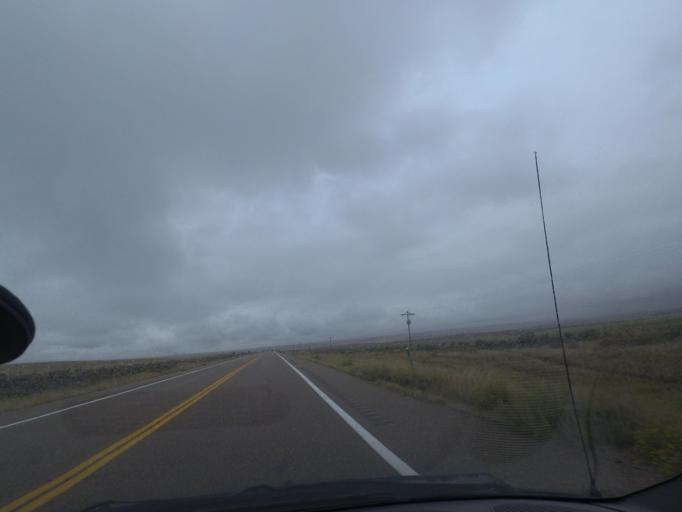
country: US
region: Colorado
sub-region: Lincoln County
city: Limon
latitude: 39.7399
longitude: -103.7329
